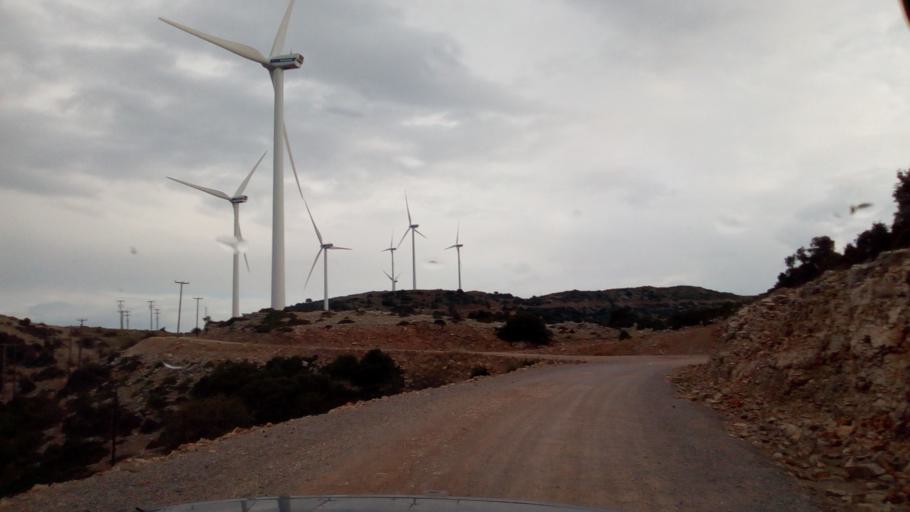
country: GR
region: West Greece
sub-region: Nomos Achaias
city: Kamarai
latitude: 38.4200
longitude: 22.0390
